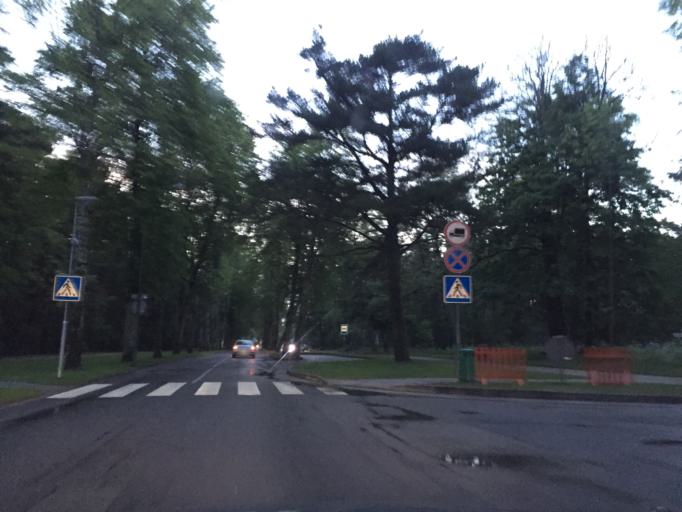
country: LT
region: Klaipedos apskritis
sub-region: Klaipeda
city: Palanga
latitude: 55.9077
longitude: 21.0621
